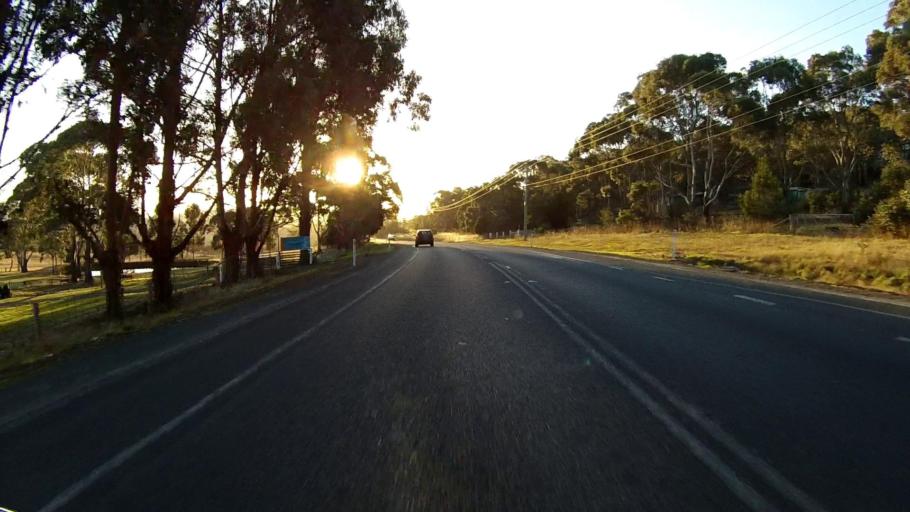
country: AU
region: Tasmania
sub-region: Sorell
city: Sorell
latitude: -42.7855
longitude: 147.6045
